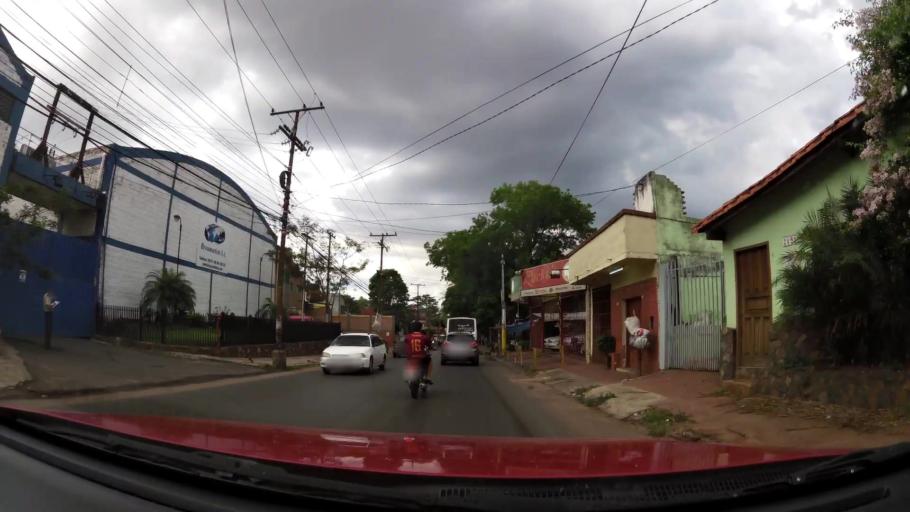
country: PY
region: Central
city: Villa Elisa
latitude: -25.3437
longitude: -57.5676
